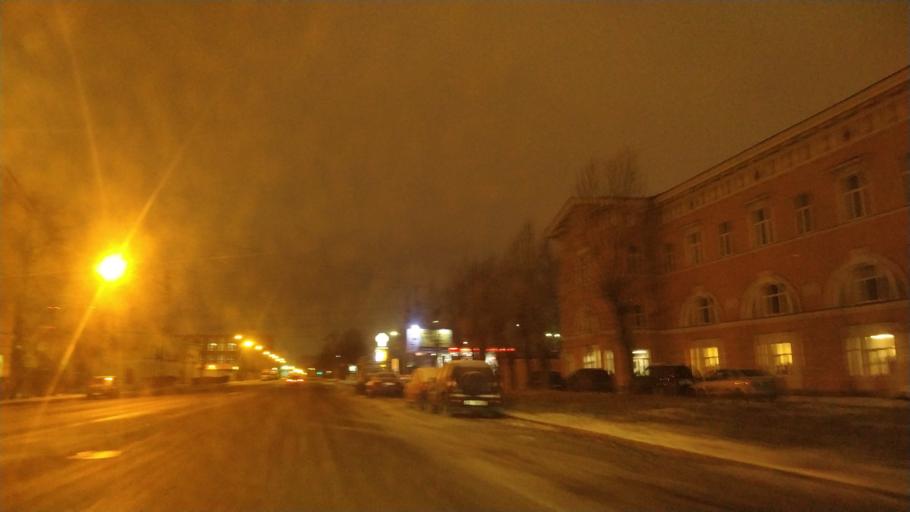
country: RU
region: St.-Petersburg
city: Kupchino
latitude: 59.8804
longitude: 30.3455
